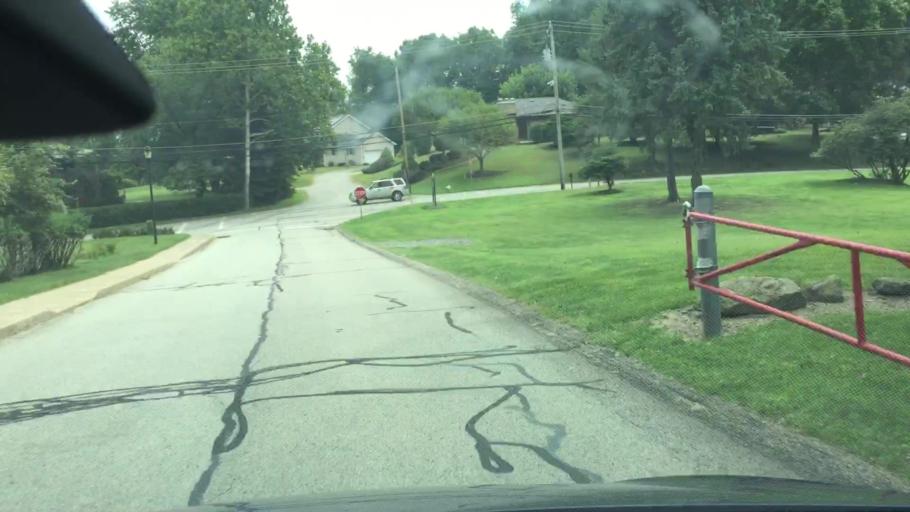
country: US
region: Pennsylvania
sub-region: Allegheny County
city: Pitcairn
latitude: 40.4186
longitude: -79.7643
